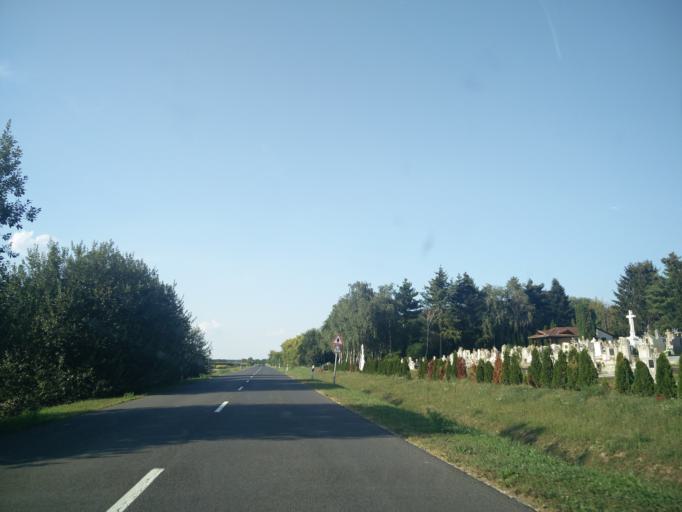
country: HU
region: Zala
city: Zalaegerszeg
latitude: 46.8703
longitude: 16.8297
